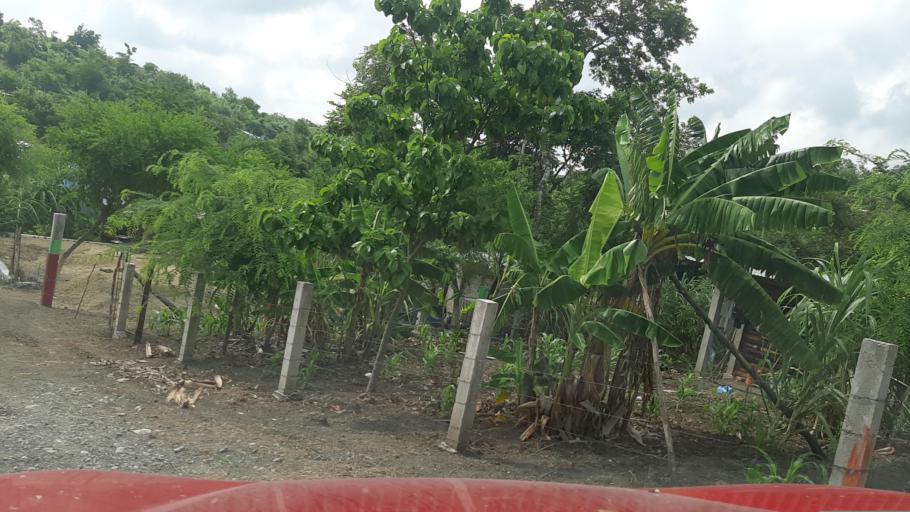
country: MX
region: Veracruz
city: Coatzintla
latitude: 20.5056
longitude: -97.4596
